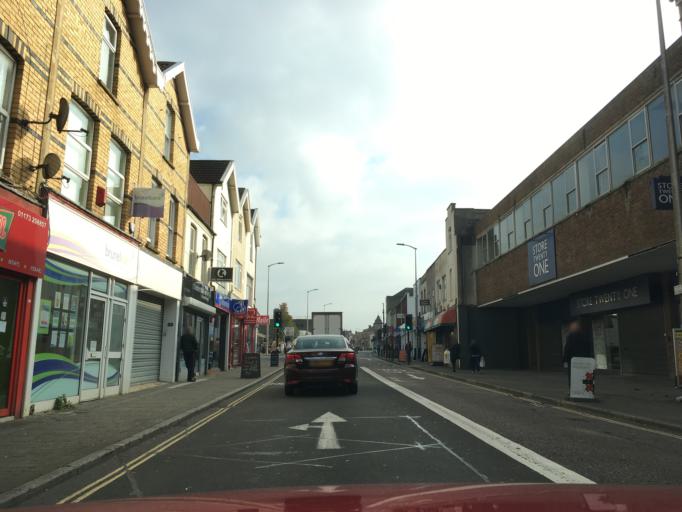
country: GB
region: England
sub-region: South Gloucestershire
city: Kingswood
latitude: 51.4629
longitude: -2.5107
